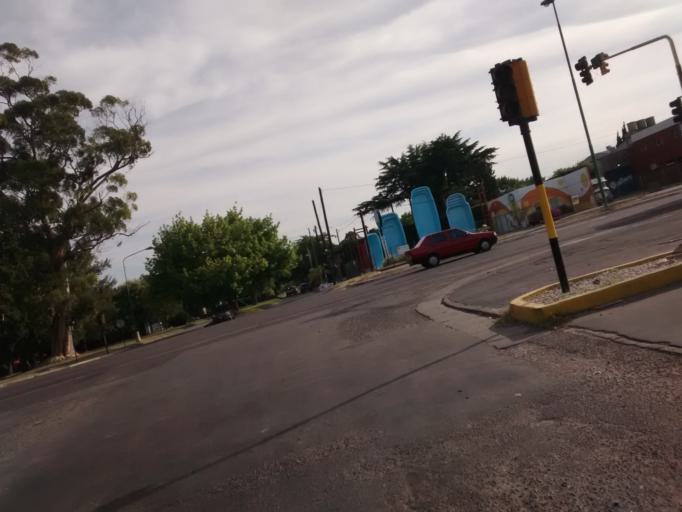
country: AR
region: Buenos Aires
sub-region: Partido de La Plata
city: La Plata
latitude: -34.8509
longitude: -58.0884
